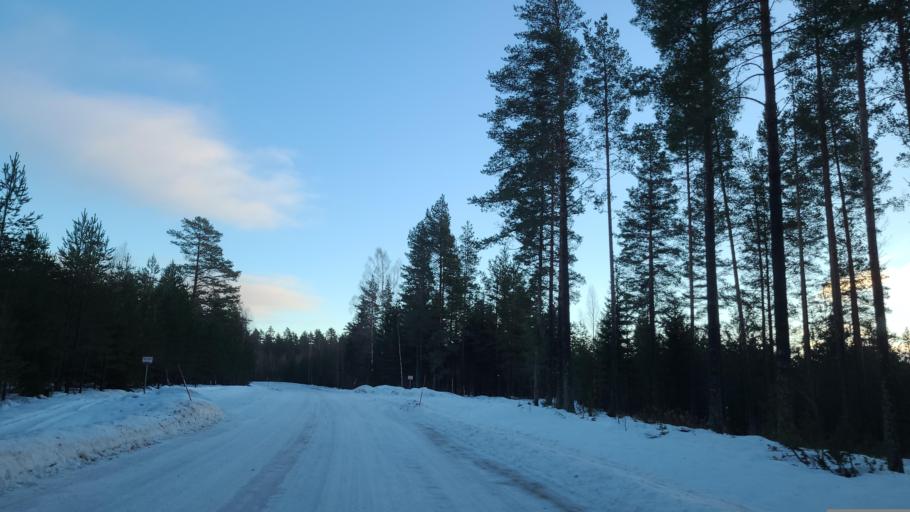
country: SE
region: Gaevleborg
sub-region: Bollnas Kommun
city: Kilafors
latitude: 61.3569
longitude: 16.6756
